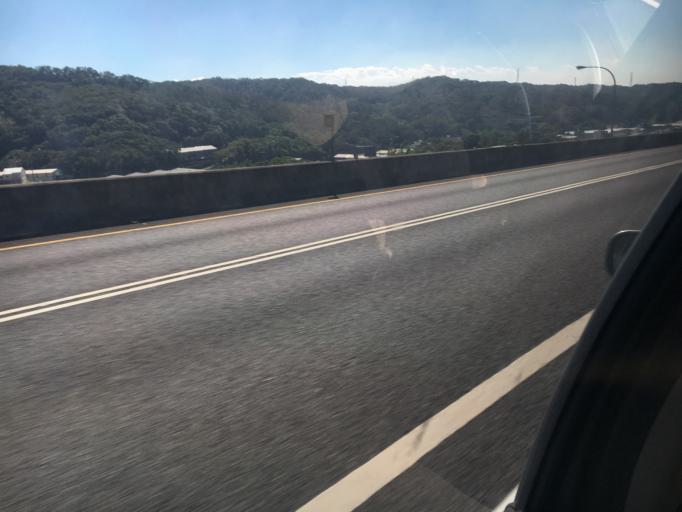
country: TW
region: Taiwan
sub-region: Taoyuan
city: Taoyuan
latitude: 25.0577
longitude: 121.3294
